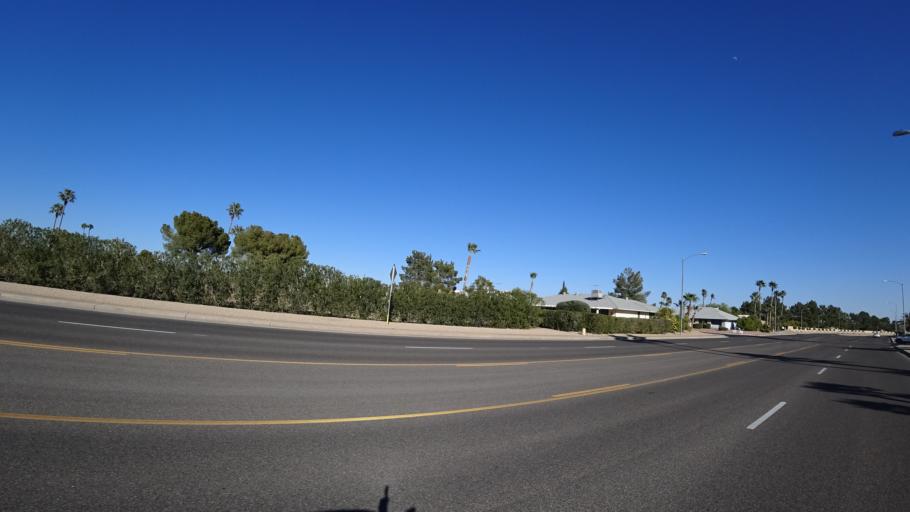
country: US
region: Arizona
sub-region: Maricopa County
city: Sun City West
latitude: 33.6776
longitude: -112.3439
